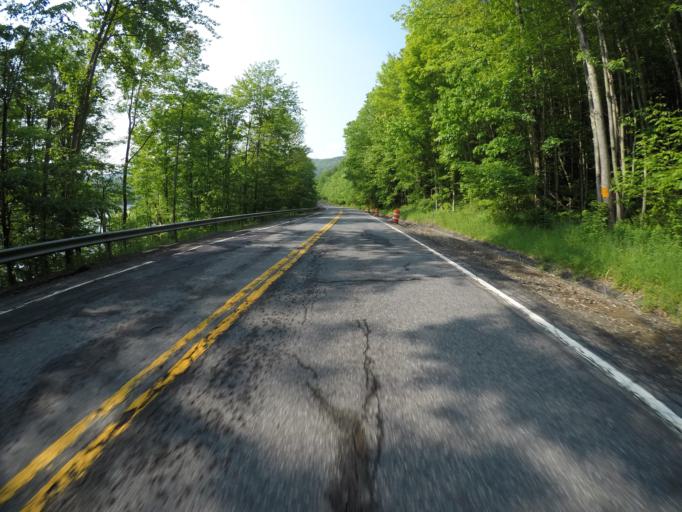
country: US
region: New York
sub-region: Sullivan County
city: Livingston Manor
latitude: 42.0947
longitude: -74.7995
